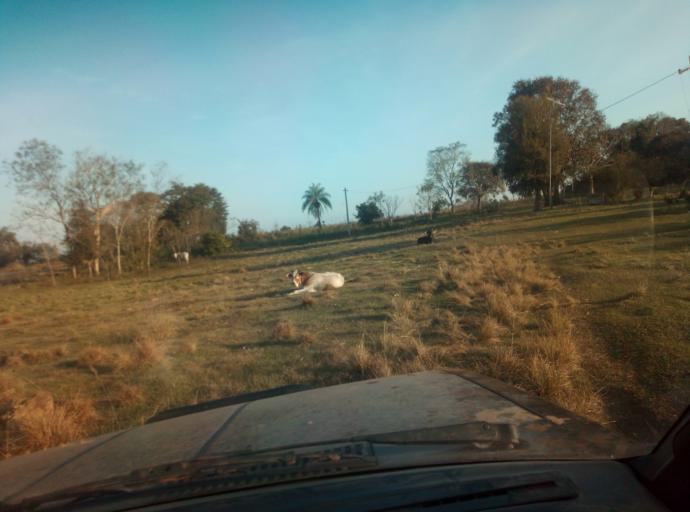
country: PY
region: Caaguazu
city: Doctor Cecilio Baez
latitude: -25.1540
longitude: -56.2359
